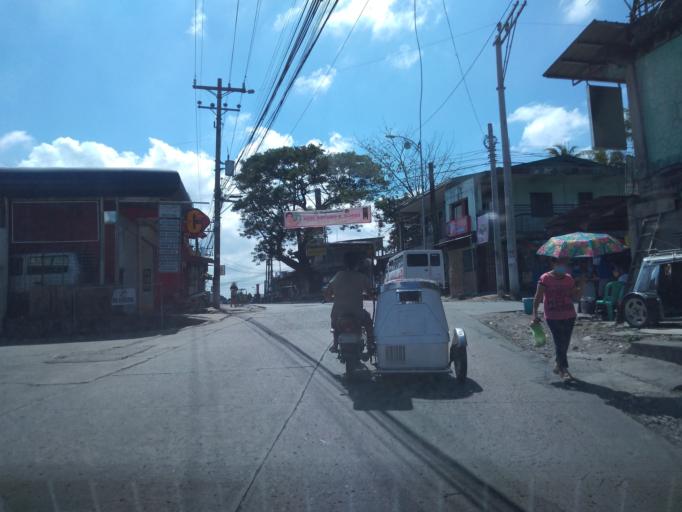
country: PH
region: Central Luzon
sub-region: Province of Bulacan
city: Bitungol
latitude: 14.8545
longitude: 121.0725
